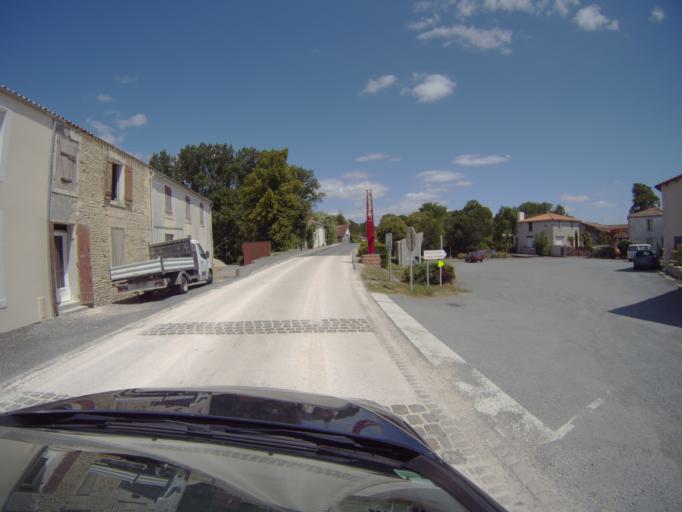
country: FR
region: Poitou-Charentes
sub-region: Departement des Deux-Sevres
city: Saint-Hilaire-la-Palud
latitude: 46.2515
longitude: -0.7624
